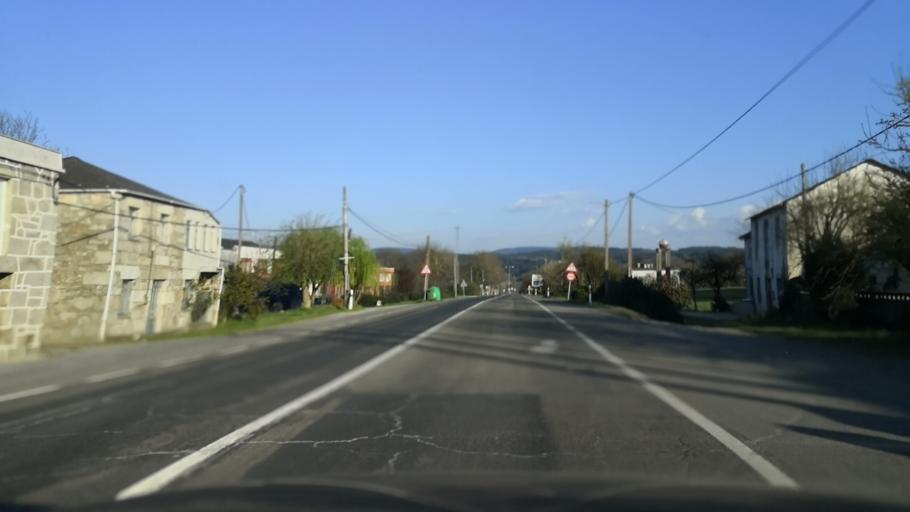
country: ES
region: Galicia
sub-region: Provincia de Lugo
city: Corgo
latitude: 42.9342
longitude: -7.4023
